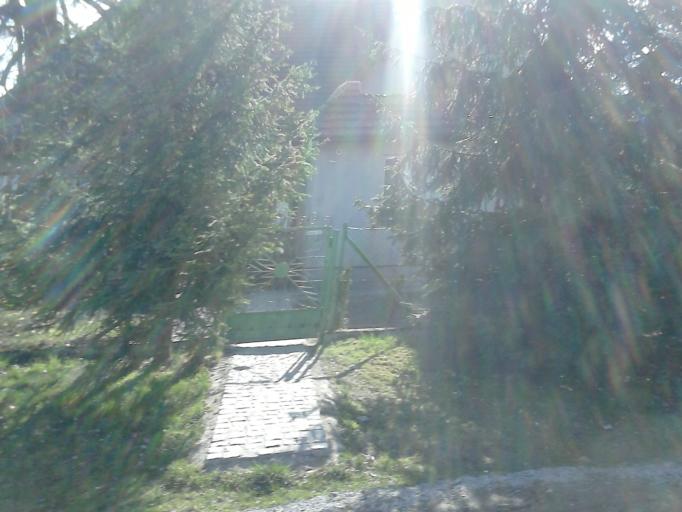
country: PL
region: Lower Silesian Voivodeship
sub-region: Powiat olesnicki
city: Dziadowa Kloda
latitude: 51.1786
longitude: 17.6859
